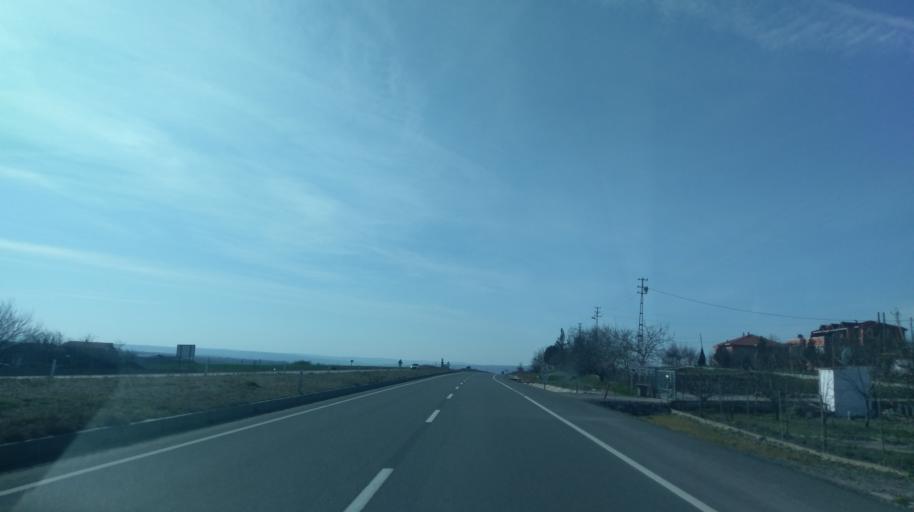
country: TR
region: Edirne
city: Hamidiye
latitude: 41.1511
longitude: 26.6622
